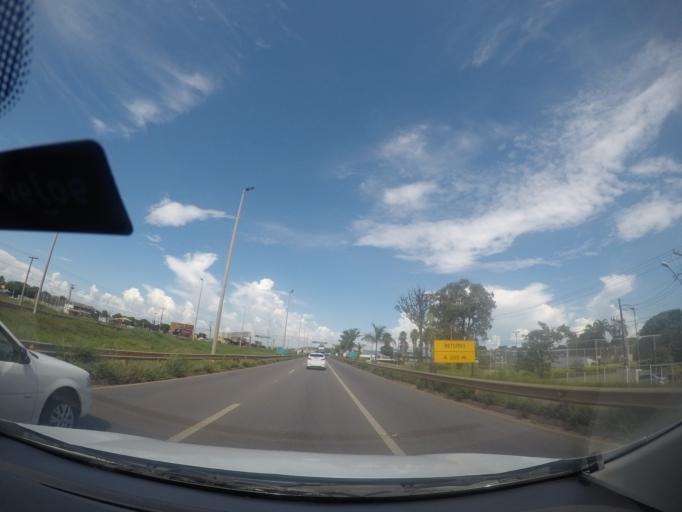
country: BR
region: Goias
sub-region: Trindade
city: Trindade
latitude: -16.6563
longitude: -49.3828
